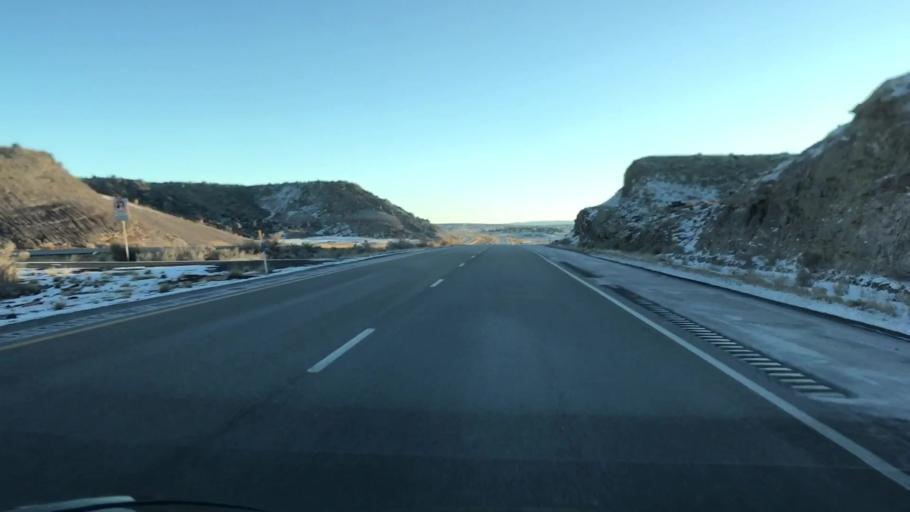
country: US
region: Utah
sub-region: Emery County
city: Ferron
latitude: 38.8167
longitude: -111.1727
